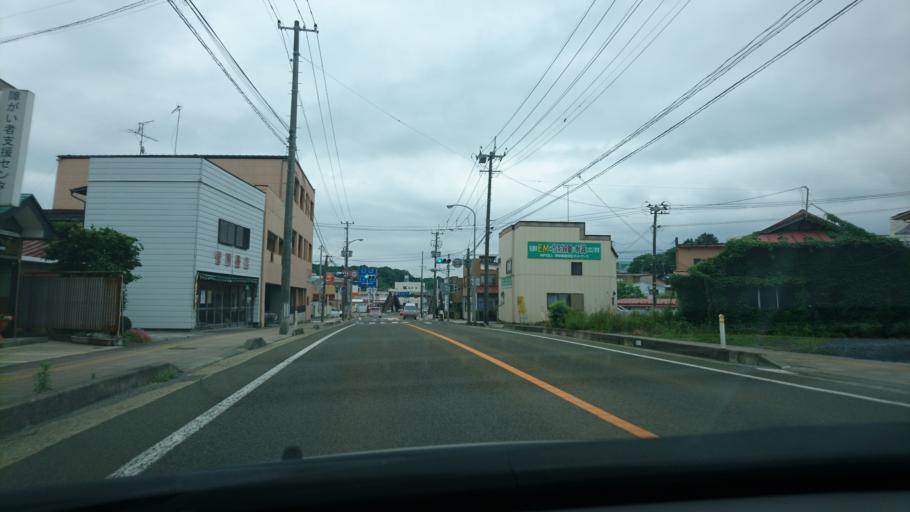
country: JP
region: Miyagi
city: Furukawa
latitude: 38.7326
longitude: 141.0227
